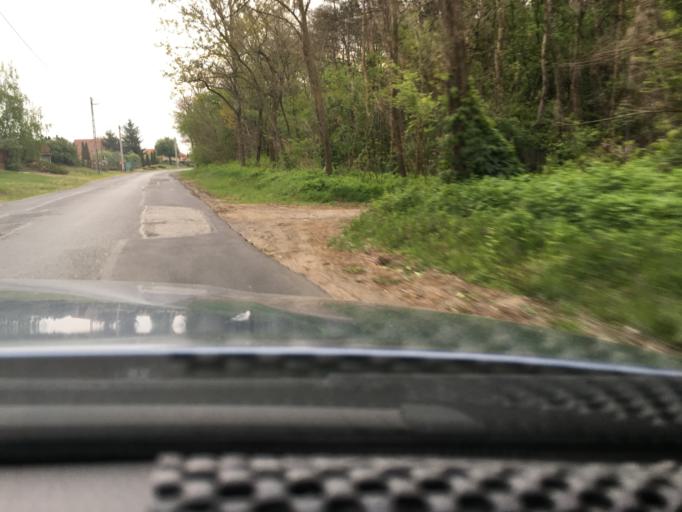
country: HU
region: Hajdu-Bihar
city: Hajdusamson
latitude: 47.5644
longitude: 21.7561
